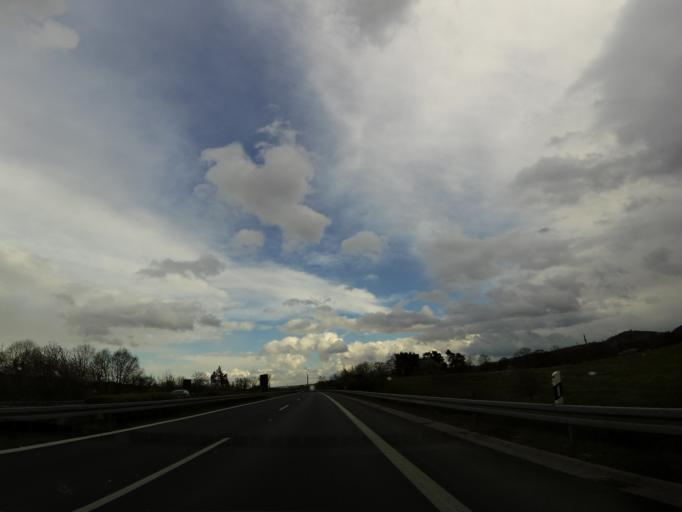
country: DE
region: Saxony-Anhalt
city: Blankenburg
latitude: 51.8170
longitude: 10.9330
